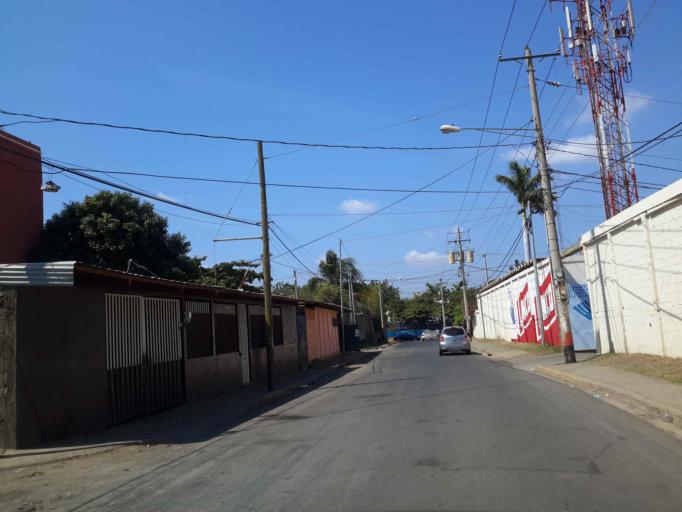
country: NI
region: Managua
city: Managua
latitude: 12.1310
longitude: -86.2795
